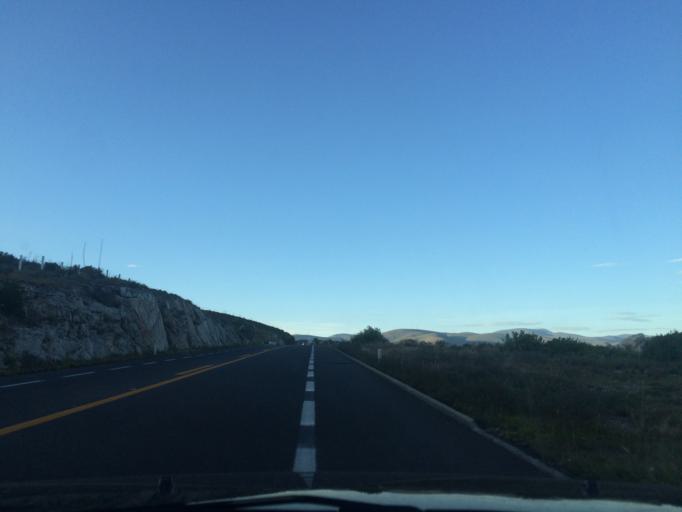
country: MX
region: Puebla
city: Cuacnopalan
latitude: 18.7905
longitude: -97.4890
